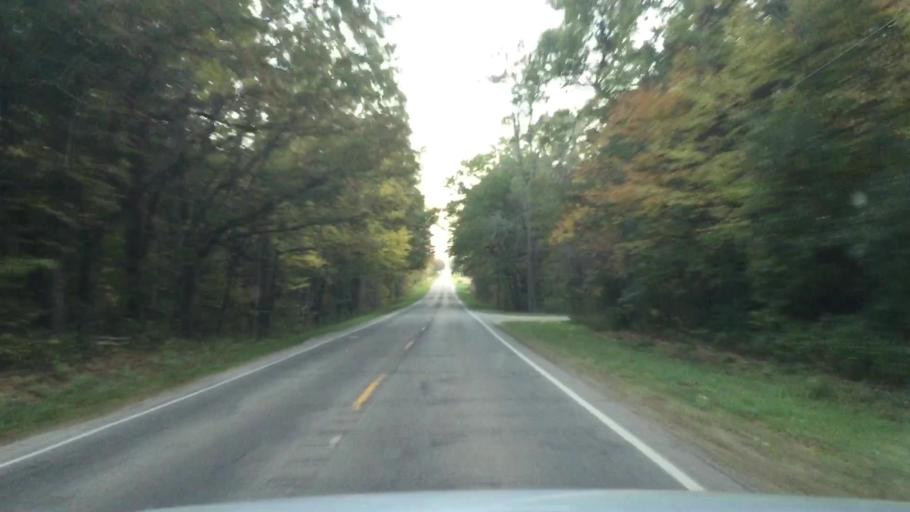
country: US
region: Michigan
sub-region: Lapeer County
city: Barnes Lake-Millers Lake
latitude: 43.1197
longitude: -83.2502
